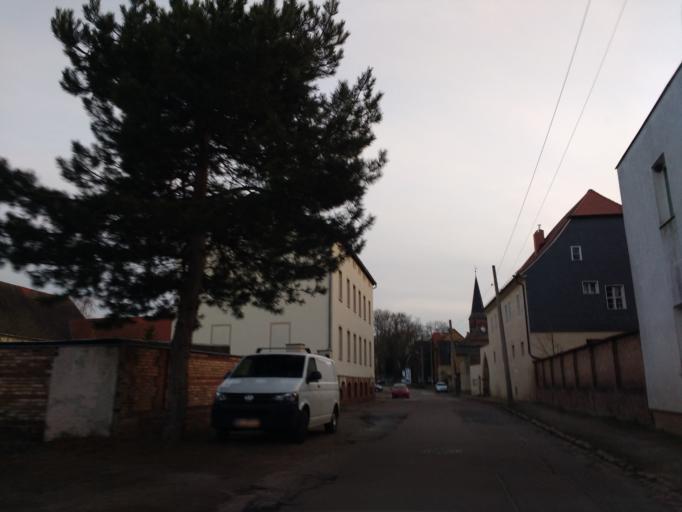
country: DE
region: Saxony-Anhalt
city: Halle (Saale)
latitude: 51.5170
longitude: 12.0112
